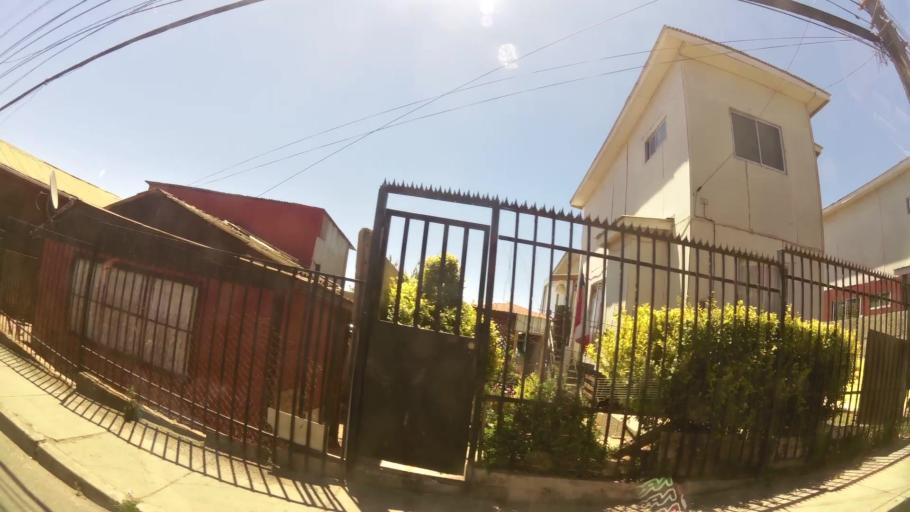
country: CL
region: Valparaiso
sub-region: Provincia de Valparaiso
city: Valparaiso
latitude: -33.0598
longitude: -71.6414
